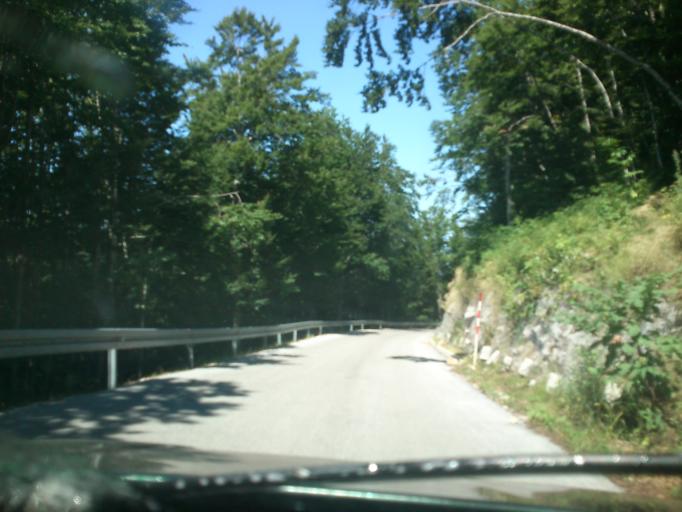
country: HR
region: Licko-Senjska
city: Senj
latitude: 44.8404
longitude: 14.9669
